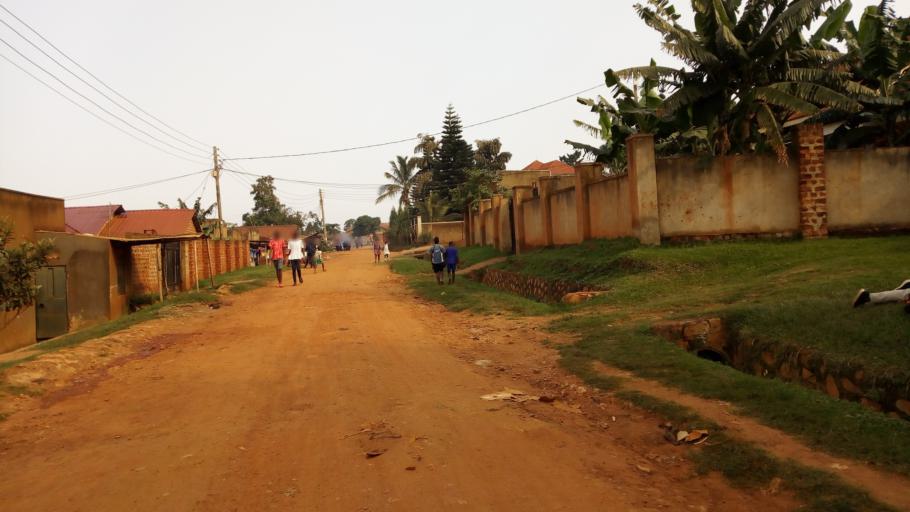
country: UG
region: Central Region
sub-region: Wakiso District
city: Kireka
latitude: 0.3128
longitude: 32.6500
